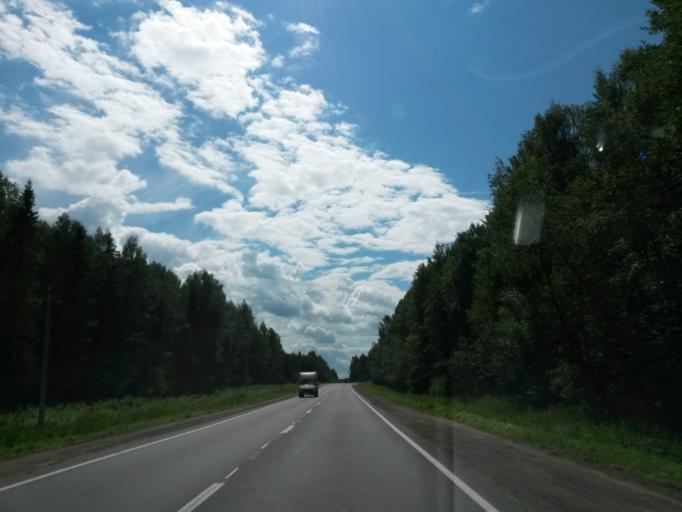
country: RU
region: Jaroslavl
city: Gavrilov-Yam
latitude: 57.2753
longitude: 39.9506
